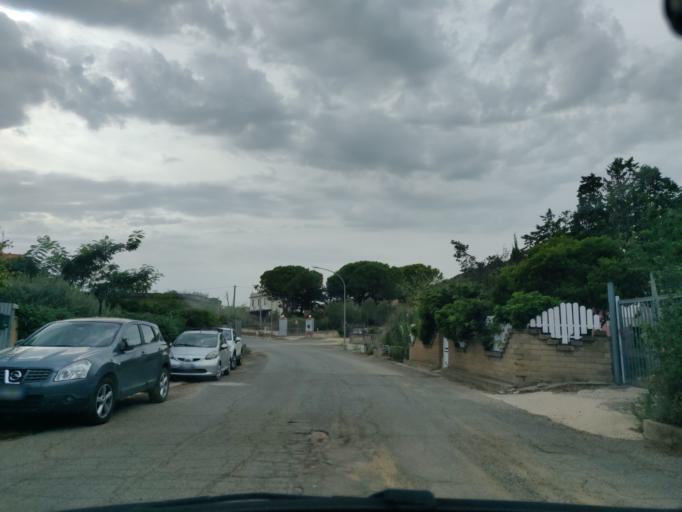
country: IT
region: Latium
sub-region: Citta metropolitana di Roma Capitale
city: Santa Marinella
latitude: 42.0422
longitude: 11.9068
